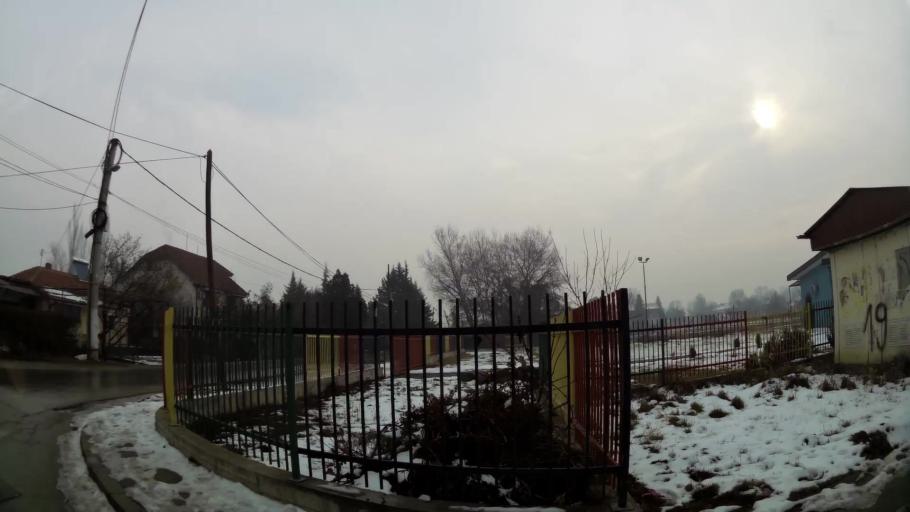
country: MK
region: Ilinden
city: Jurumleri
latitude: 41.9647
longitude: 21.5600
